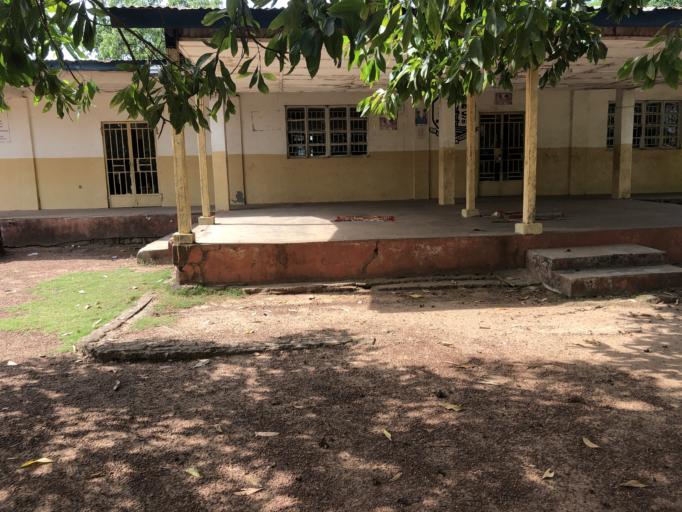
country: SL
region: Northern Province
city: Yonibana
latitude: 8.4661
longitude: -12.2231
